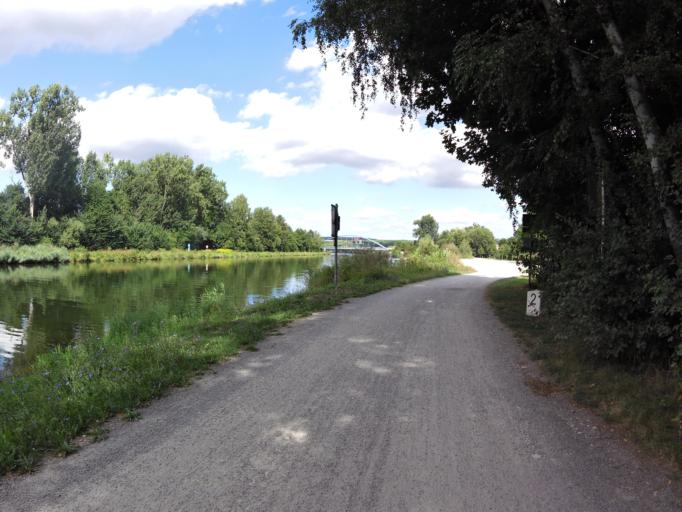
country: DE
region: Bavaria
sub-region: Regierungsbezirk Unterfranken
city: Volkach
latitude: 49.8581
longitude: 10.2238
